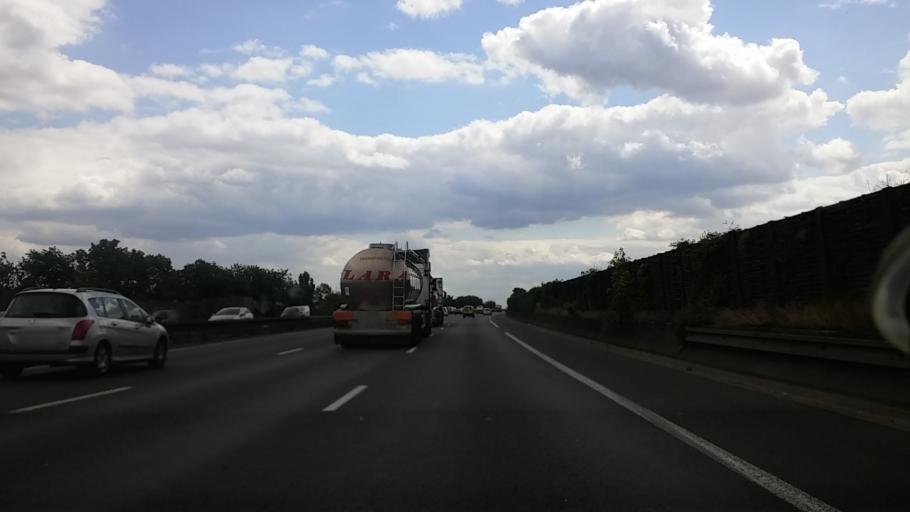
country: FR
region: Ile-de-France
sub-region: Departement de Seine-Saint-Denis
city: Aulnay-sous-Bois
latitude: 48.9390
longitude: 2.4798
